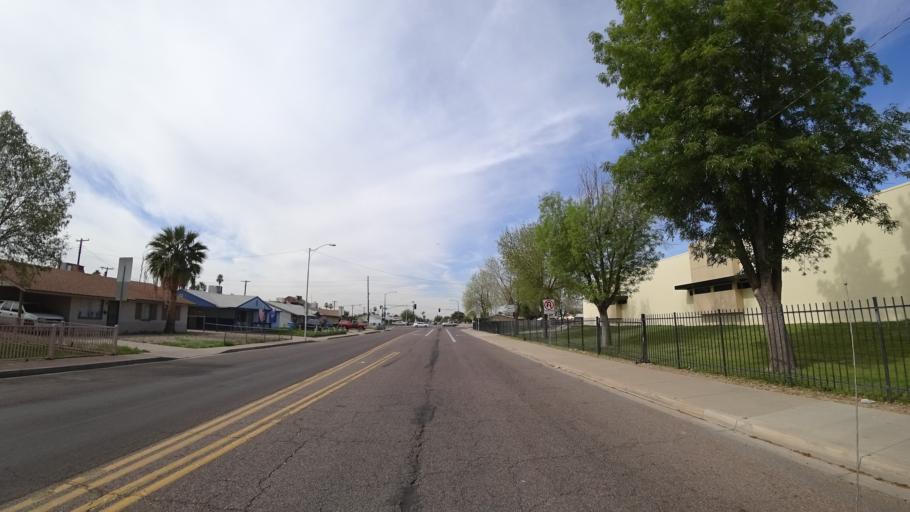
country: US
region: Arizona
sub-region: Maricopa County
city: Glendale
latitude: 33.4878
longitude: -112.1852
